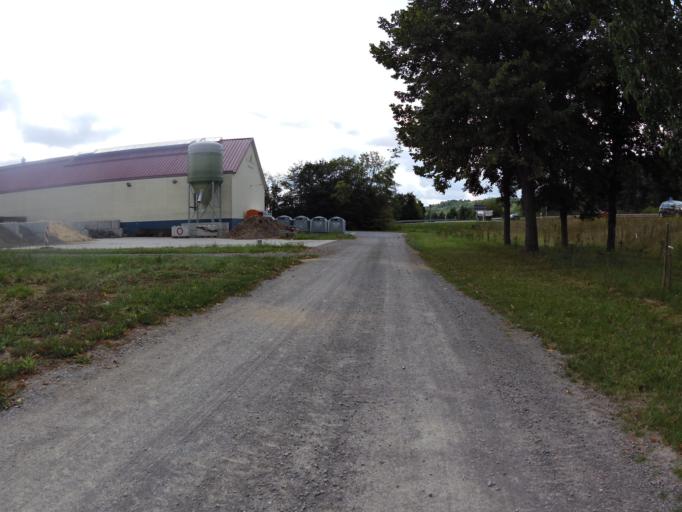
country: DE
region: Bavaria
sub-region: Regierungsbezirk Unterfranken
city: Sommerhausen
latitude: 49.6981
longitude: 10.0240
